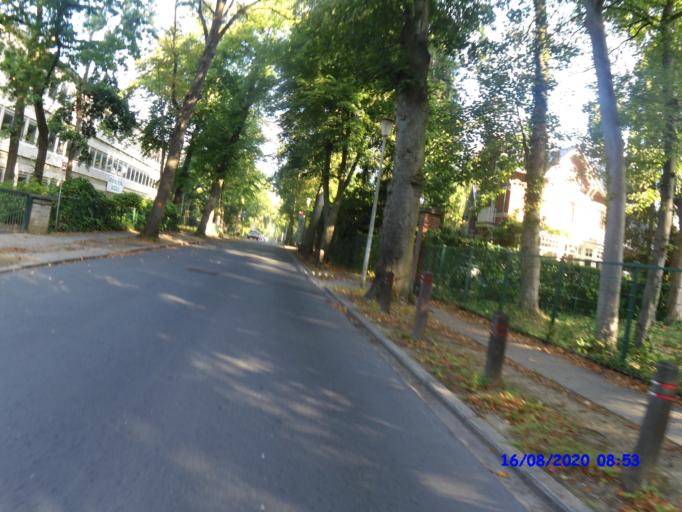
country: BE
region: Flanders
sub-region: Provincie Vlaams-Brabant
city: Linkebeek
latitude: 50.7764
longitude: 4.3395
